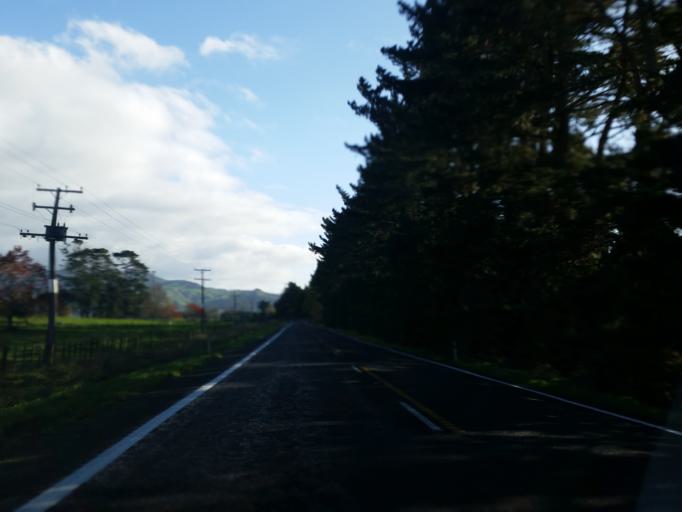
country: NZ
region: Waikato
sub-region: Hauraki District
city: Waihi
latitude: -37.4159
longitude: 175.8651
